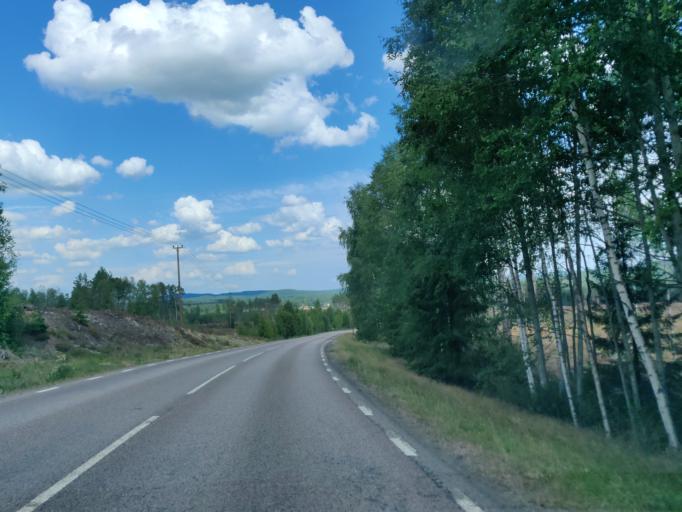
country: SE
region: Vaermland
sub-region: Hagfors Kommun
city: Hagfors
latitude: 59.8702
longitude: 13.6975
